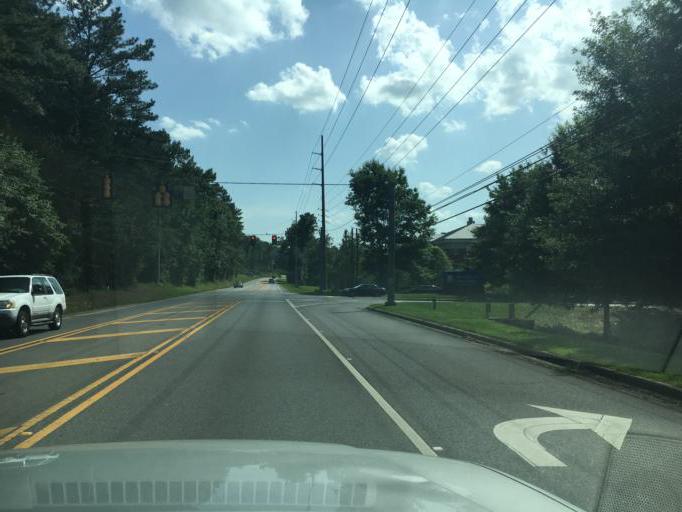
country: US
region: Alabama
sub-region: Shelby County
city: Meadowbrook
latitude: 33.3874
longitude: -86.7266
